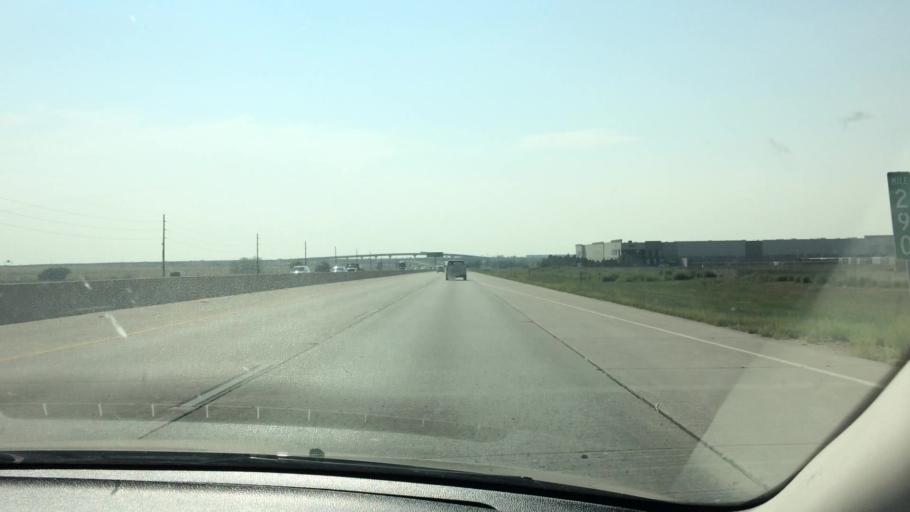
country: US
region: Colorado
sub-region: Adams County
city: Aurora
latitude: 39.7405
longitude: -104.7005
